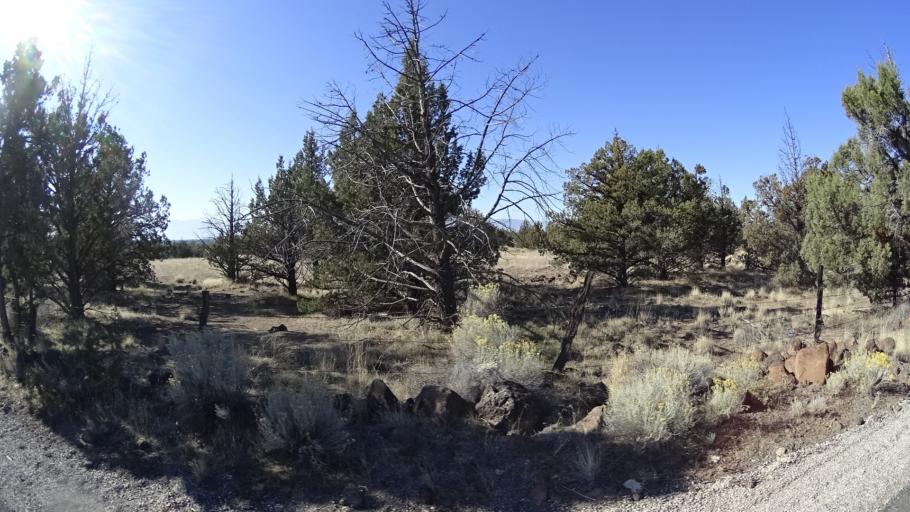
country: US
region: California
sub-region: Siskiyou County
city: Weed
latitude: 41.6049
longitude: -122.3076
